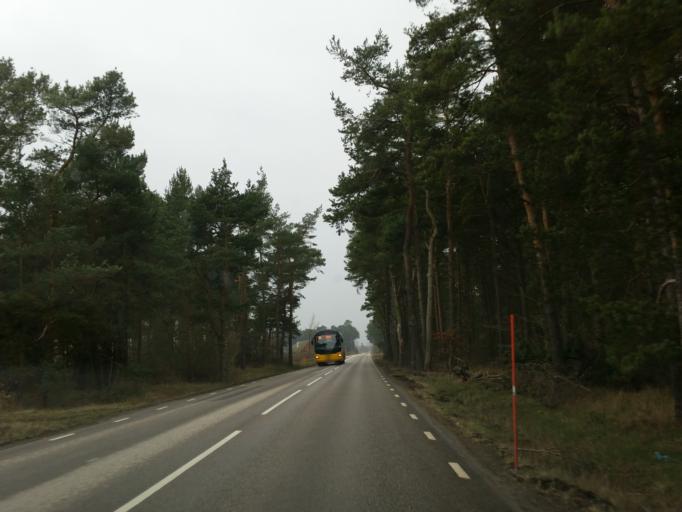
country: SE
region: Kalmar
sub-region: Morbylanga Kommun
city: Moerbylanga
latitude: 56.5362
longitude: 16.4098
